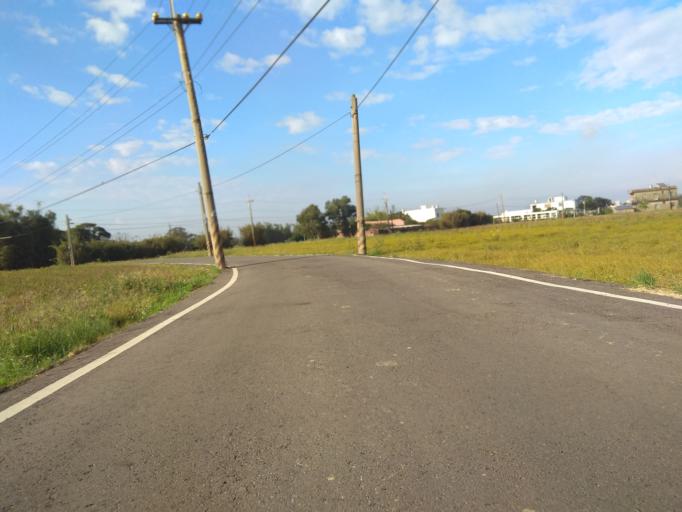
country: TW
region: Taiwan
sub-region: Hsinchu
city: Zhubei
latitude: 24.9787
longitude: 121.0635
